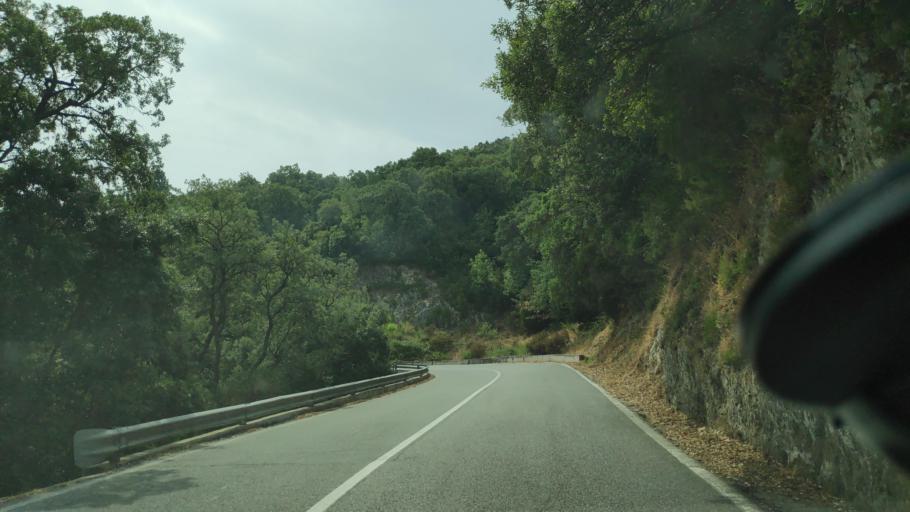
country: IT
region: Calabria
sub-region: Provincia di Catanzaro
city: San Sostene
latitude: 38.6387
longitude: 16.5097
